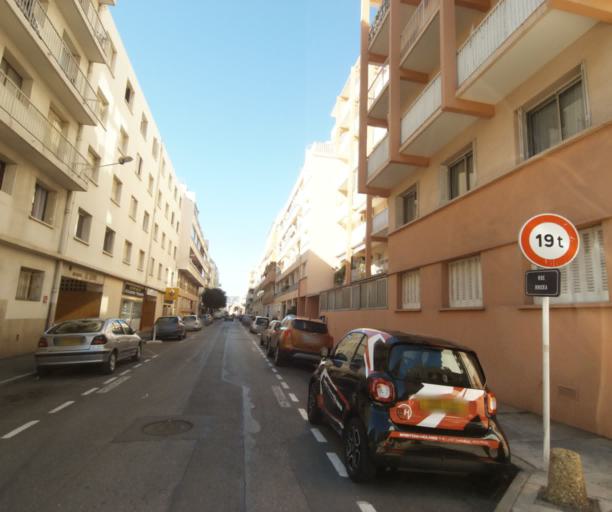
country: FR
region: Provence-Alpes-Cote d'Azur
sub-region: Departement des Alpes-Maritimes
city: Antibes
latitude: 43.5713
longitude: 7.1070
